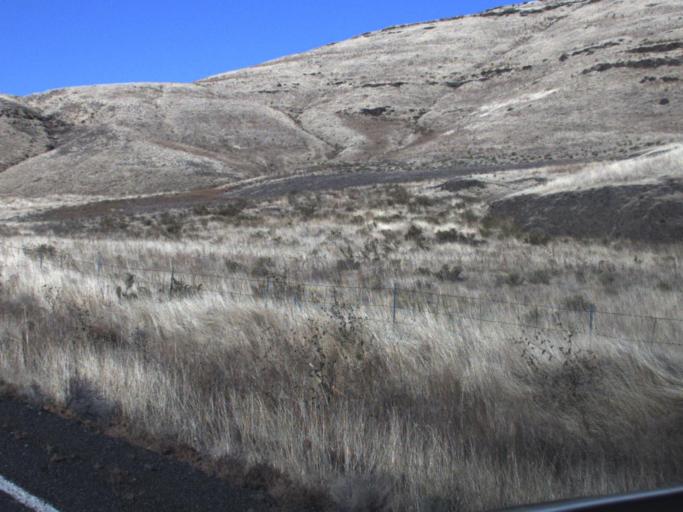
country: US
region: Washington
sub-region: Franklin County
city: Connell
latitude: 46.5786
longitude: -118.5383
